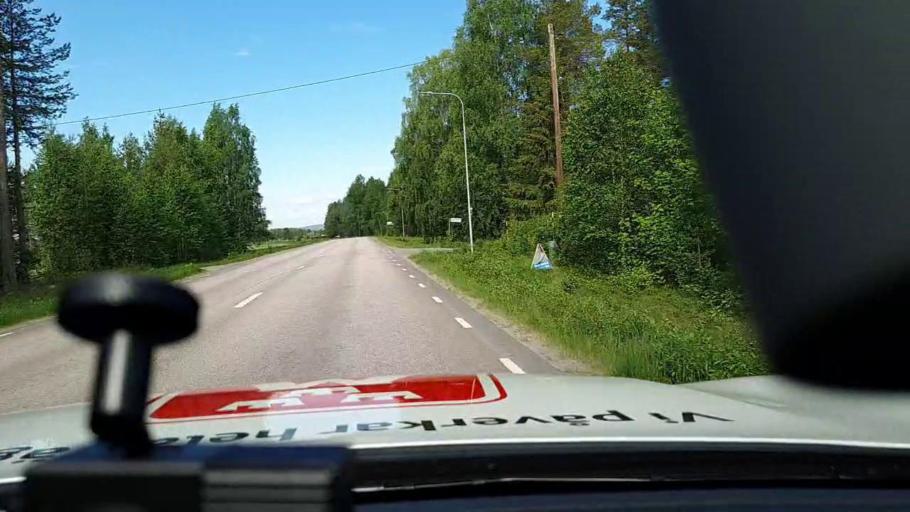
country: SE
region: Norrbotten
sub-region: Lulea Kommun
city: Sodra Sunderbyn
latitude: 65.6473
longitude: 21.8804
